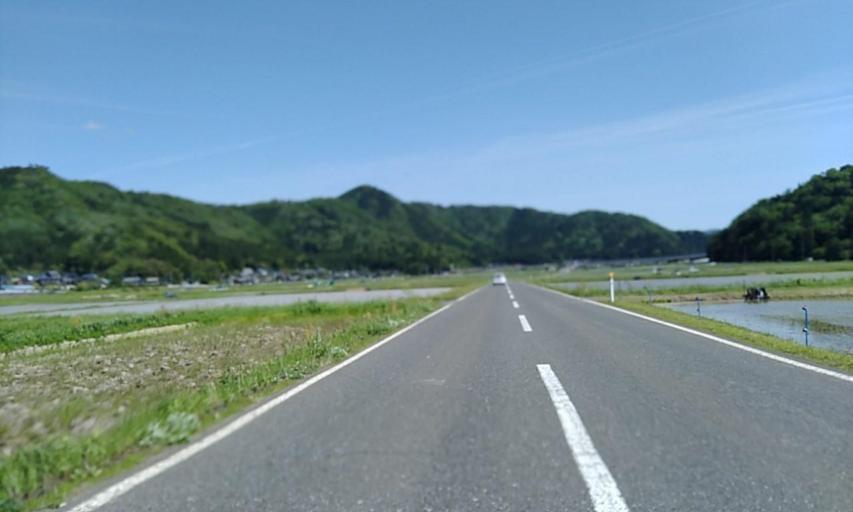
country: JP
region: Fukui
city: Obama
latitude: 35.5203
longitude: 135.8619
